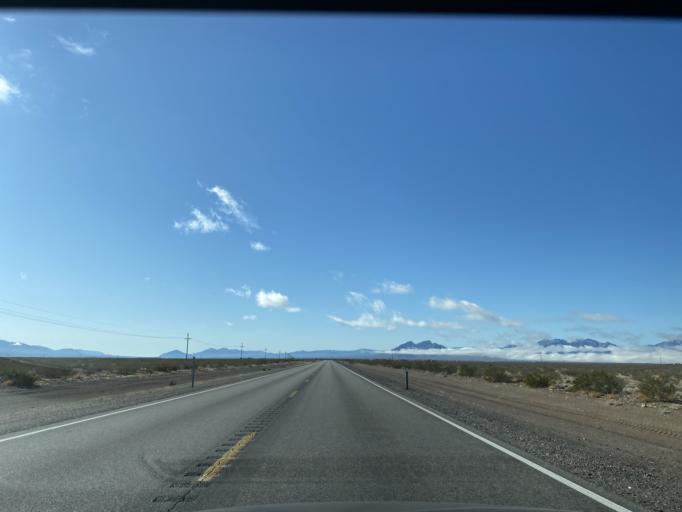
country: US
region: Nevada
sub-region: Nye County
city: Beatty
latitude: 36.5593
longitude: -116.4154
